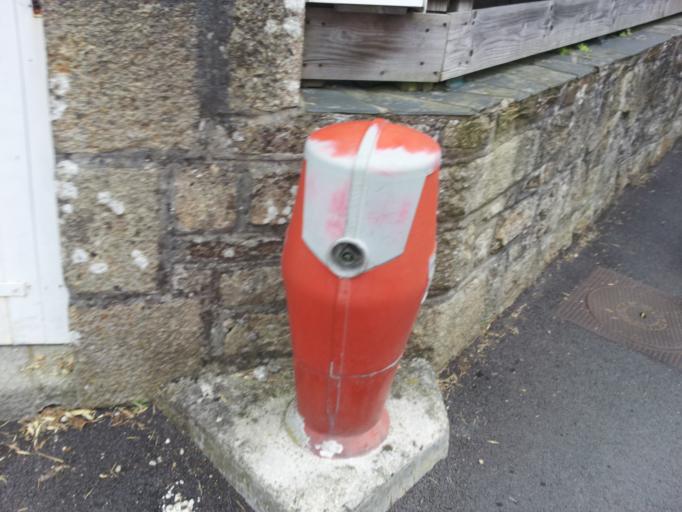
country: FR
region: Brittany
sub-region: Departement du Finistere
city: Carantec
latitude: 48.6664
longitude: -3.9134
